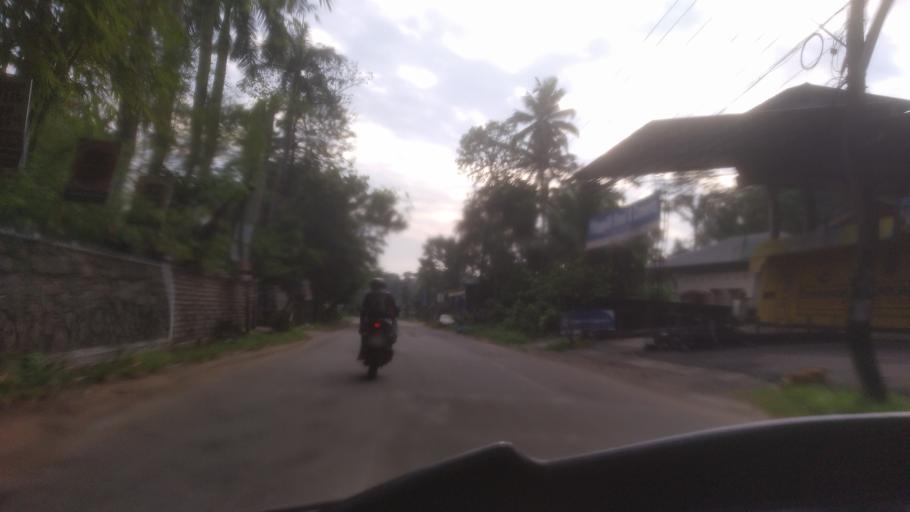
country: IN
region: Kerala
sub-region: Ernakulam
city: Kotamangalam
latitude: 10.0689
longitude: 76.6184
